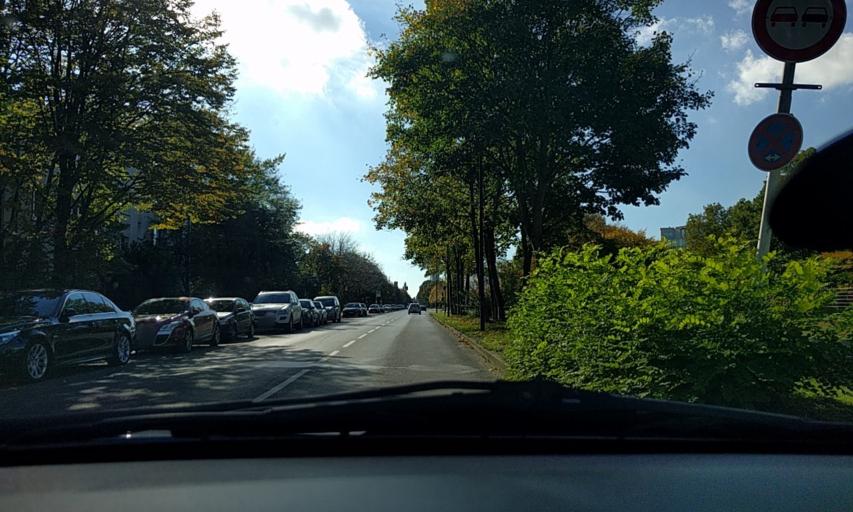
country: DE
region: North Rhine-Westphalia
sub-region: Regierungsbezirk Dusseldorf
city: Ratingen
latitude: 51.2586
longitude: 6.8144
